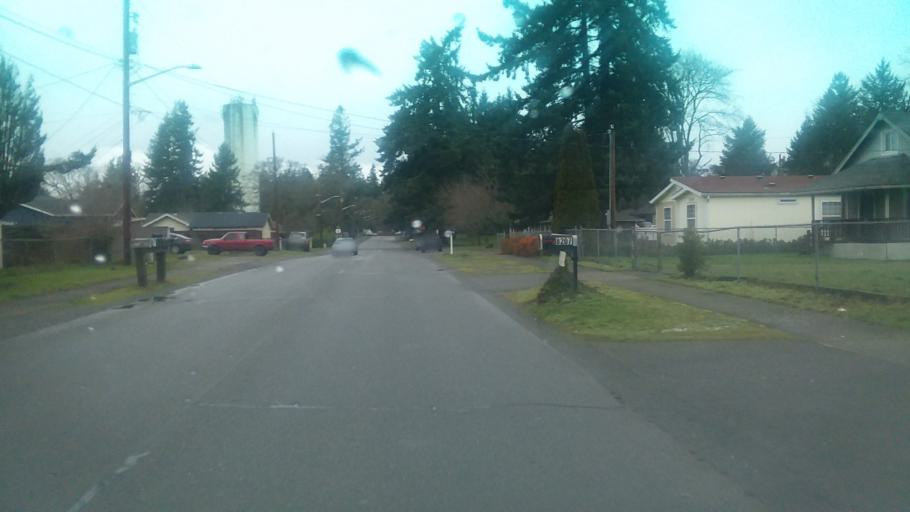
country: US
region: Washington
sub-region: Pierce County
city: Fort Lewis
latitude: 47.1256
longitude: -122.5480
